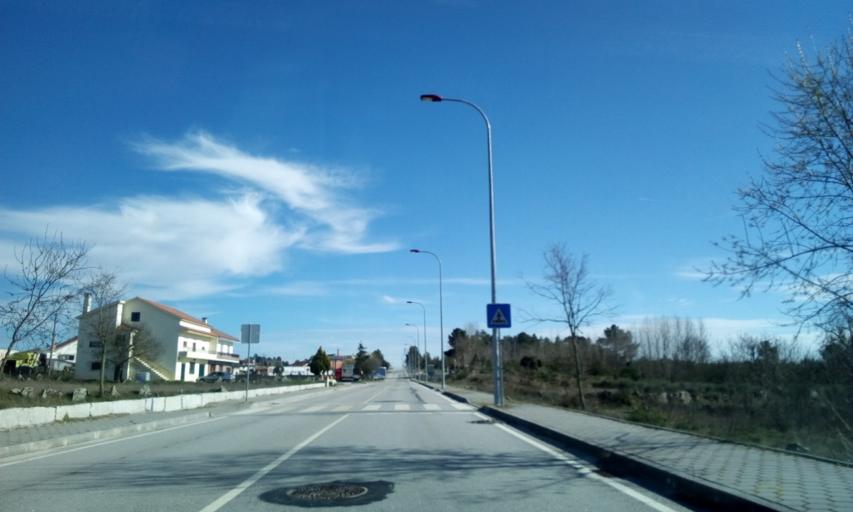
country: PT
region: Guarda
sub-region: Pinhel
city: Pinhel
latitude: 40.6009
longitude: -6.9994
